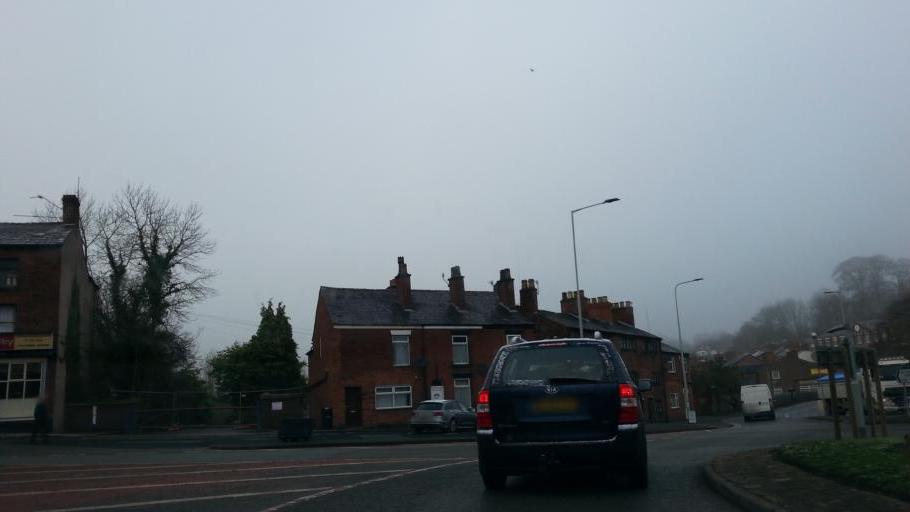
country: GB
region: England
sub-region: Cheshire East
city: Congleton
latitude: 53.1660
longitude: -2.2125
